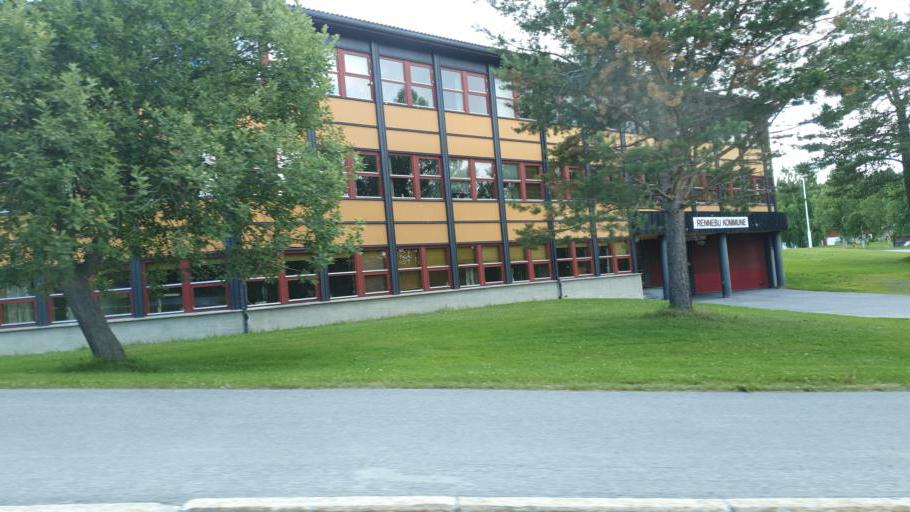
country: NO
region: Sor-Trondelag
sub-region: Rennebu
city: Berkak
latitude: 62.8288
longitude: 10.0042
